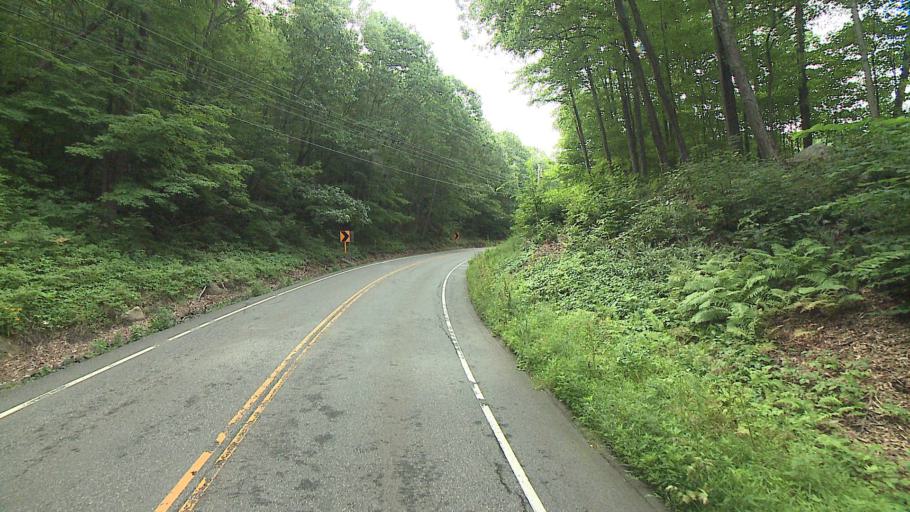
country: US
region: Connecticut
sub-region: Litchfield County
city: Kent
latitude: 41.7209
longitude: -73.4519
